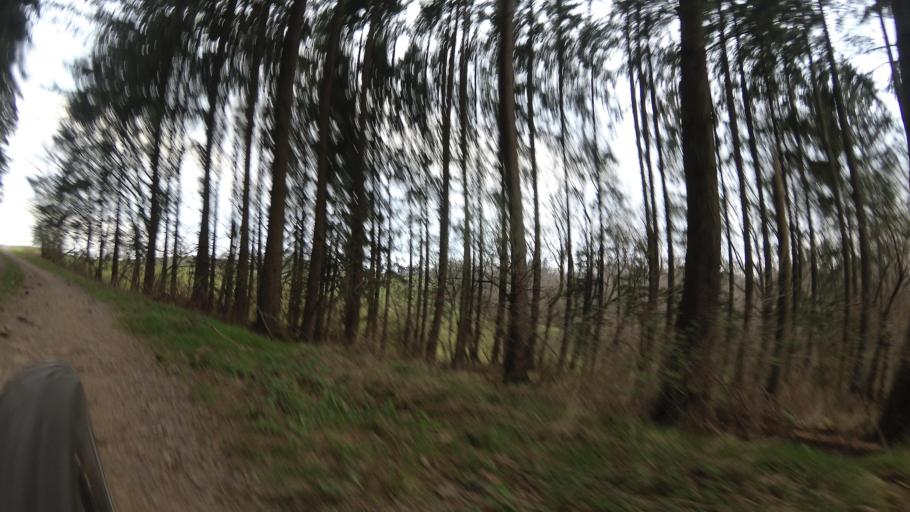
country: DE
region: Rheinland-Pfalz
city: Gimbweiler
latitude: 49.5929
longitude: 7.1894
